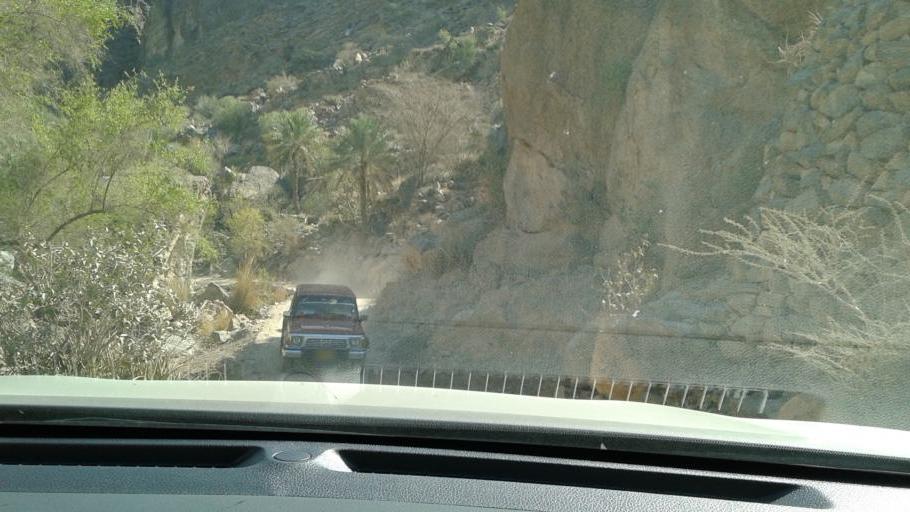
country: OM
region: Al Batinah
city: Bayt al `Awabi
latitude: 23.1973
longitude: 57.3903
